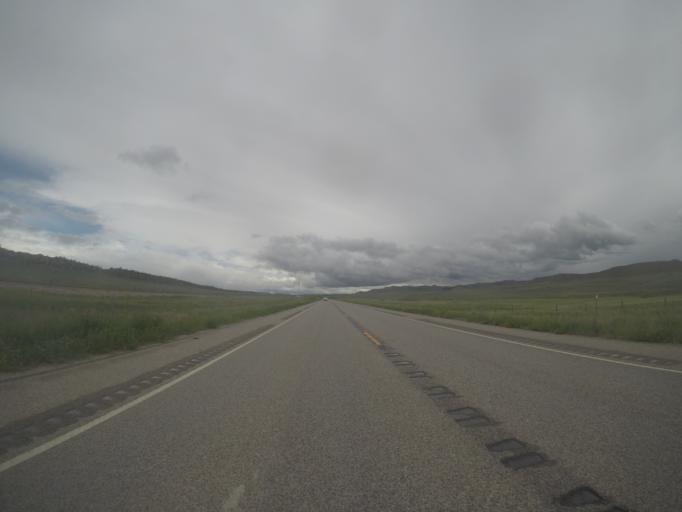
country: US
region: Wyoming
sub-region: Park County
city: Powell
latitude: 45.1601
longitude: -108.8224
